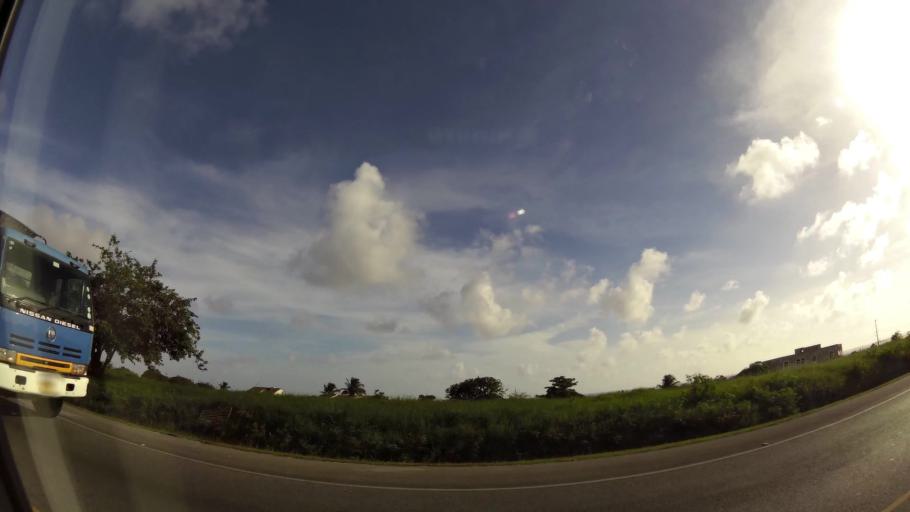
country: BB
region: Christ Church
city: Oistins
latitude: 13.0765
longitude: -59.5647
